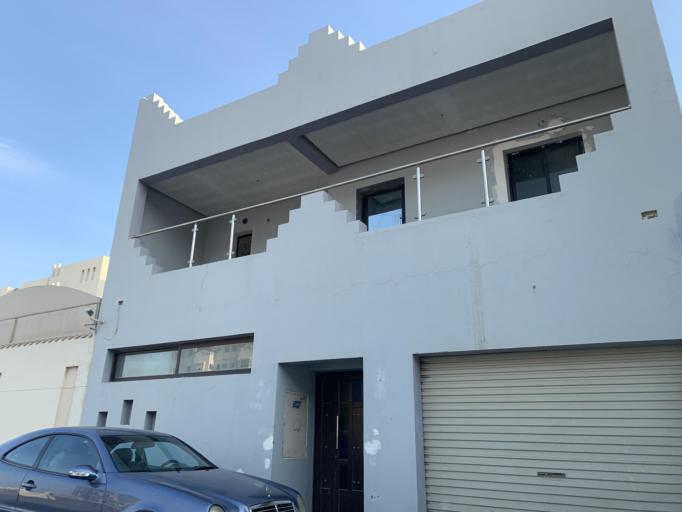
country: BH
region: Central Governorate
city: Madinat Hamad
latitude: 26.1203
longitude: 50.4889
